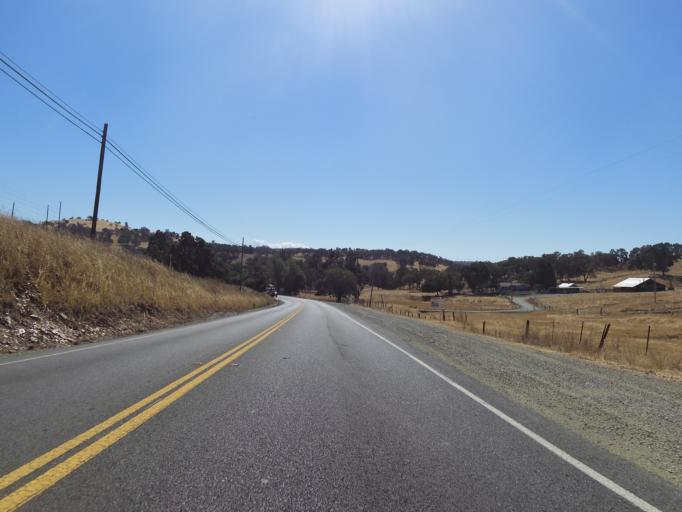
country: US
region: California
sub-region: Amador County
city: Plymouth
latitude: 38.4444
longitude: -120.8600
